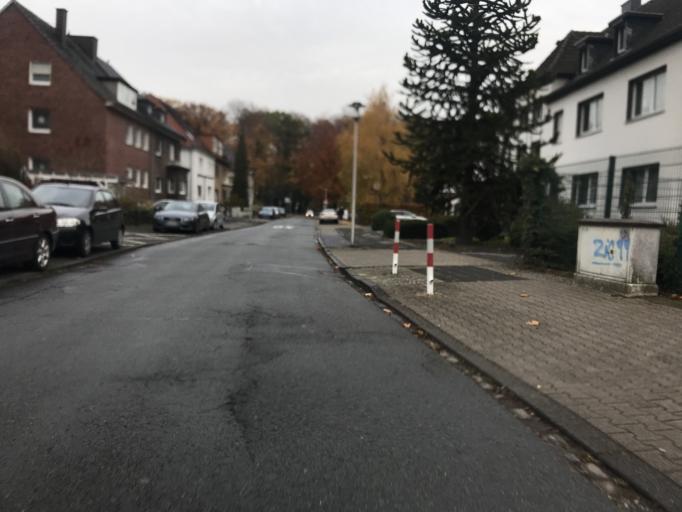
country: DE
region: North Rhine-Westphalia
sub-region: Regierungsbezirk Arnsberg
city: Hamm
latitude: 51.6886
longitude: 7.8475
